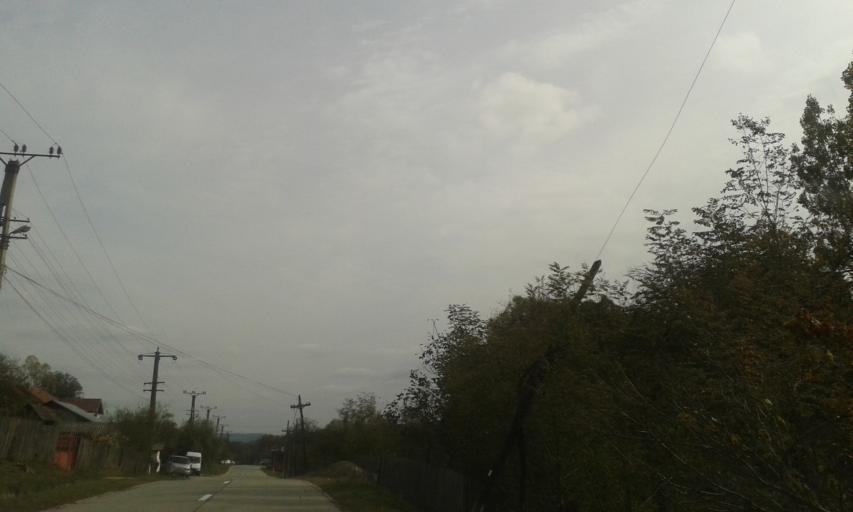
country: RO
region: Valcea
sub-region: Comuna Gradistea
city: Gradistea
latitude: 44.9120
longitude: 23.7844
